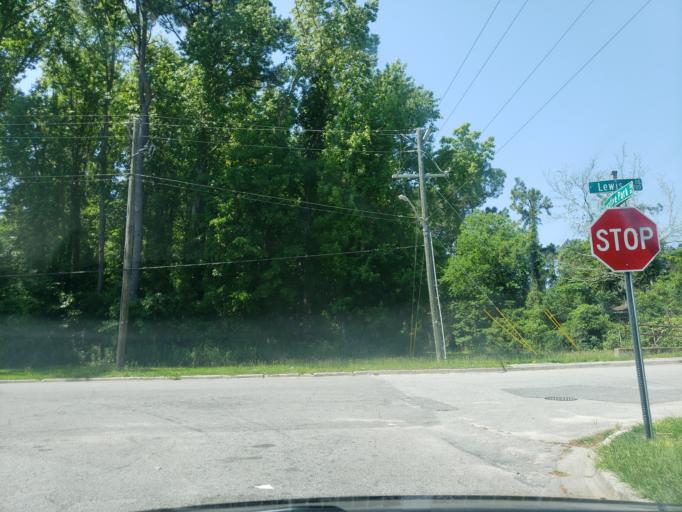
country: US
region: Georgia
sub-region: Chatham County
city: Montgomery
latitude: 31.9952
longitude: -81.1335
